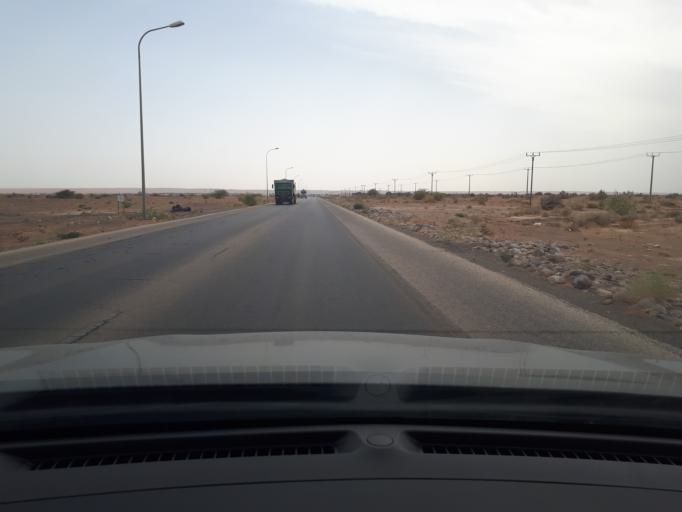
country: OM
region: Ash Sharqiyah
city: Badiyah
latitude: 22.4583
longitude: 58.8459
